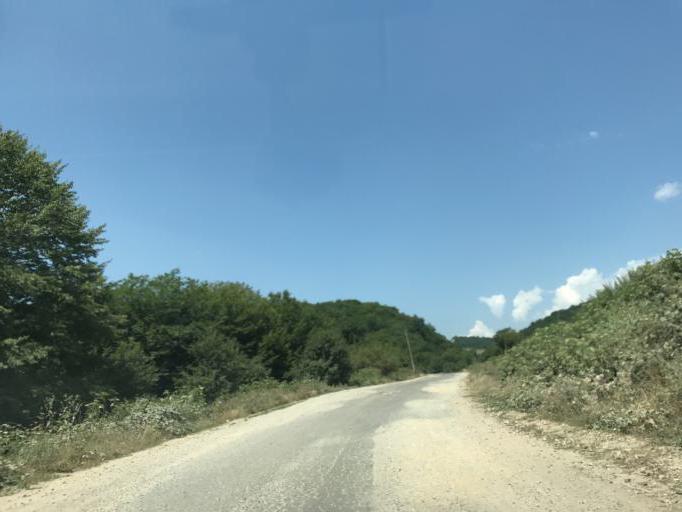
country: AZ
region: Tartar Rayon
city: Martakert
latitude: 40.1042
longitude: 46.6602
